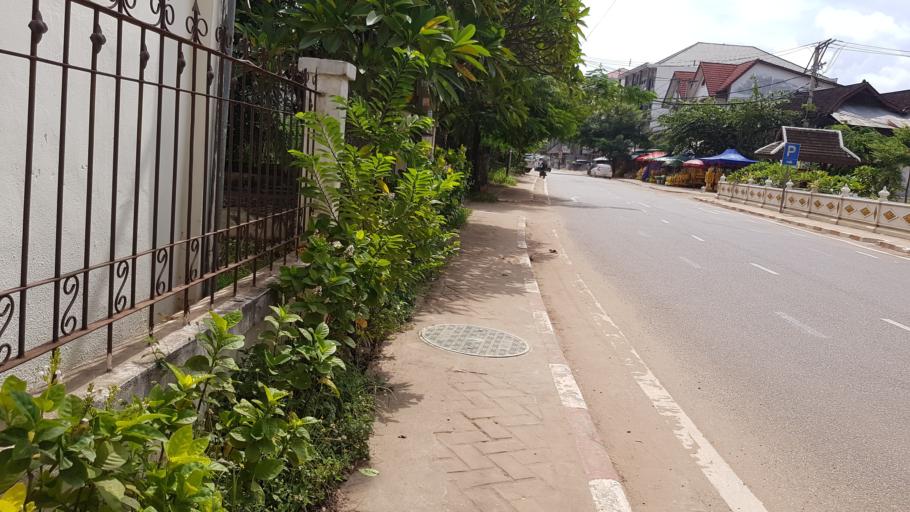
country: LA
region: Vientiane
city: Vientiane
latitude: 17.9588
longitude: 102.6158
